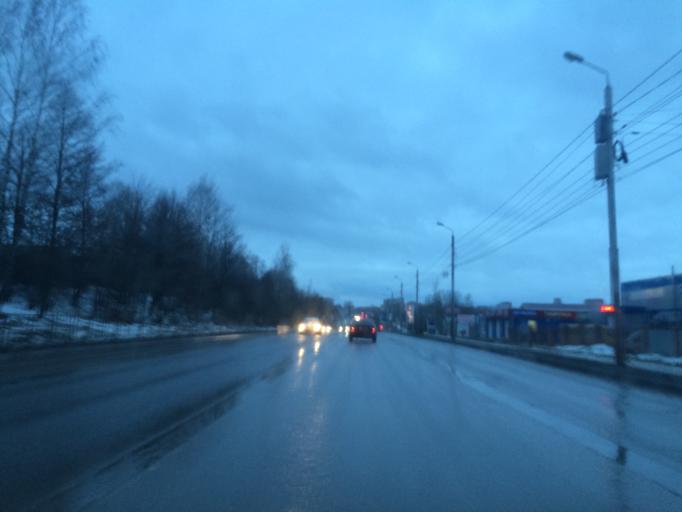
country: RU
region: Tula
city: Tula
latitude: 54.1646
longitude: 37.6246
